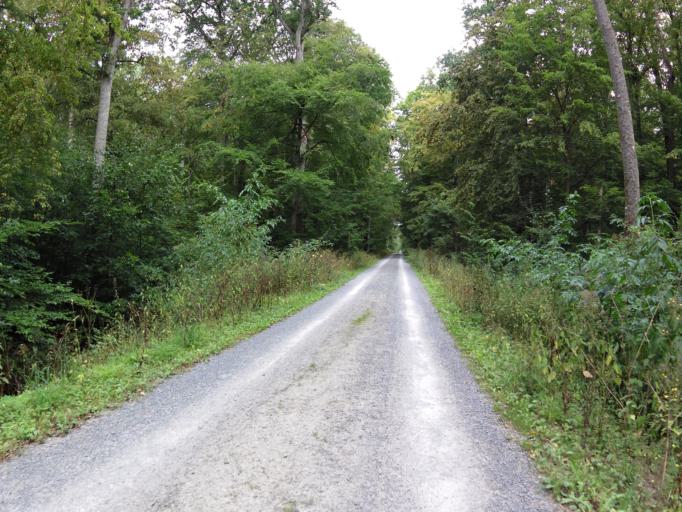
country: DE
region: Bavaria
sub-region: Regierungsbezirk Unterfranken
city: Kleinrinderfeld
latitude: 49.7195
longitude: 9.8315
